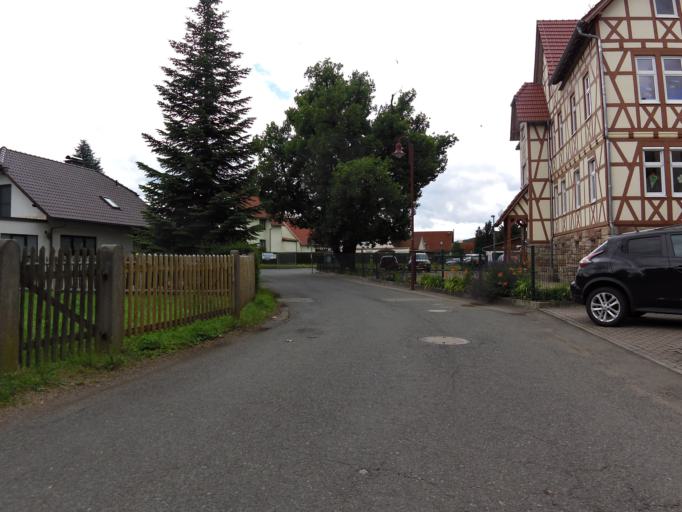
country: DE
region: Thuringia
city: Schmalkalden
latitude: 50.7201
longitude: 10.4245
